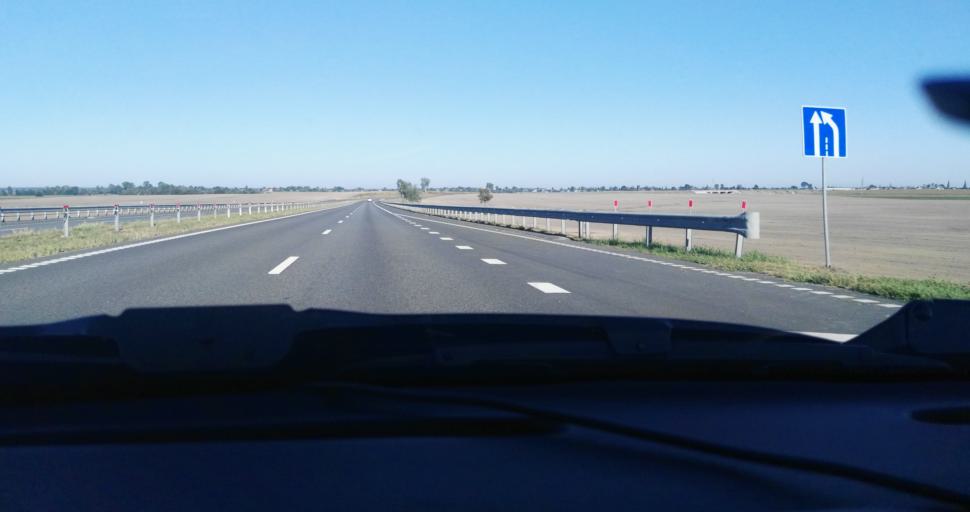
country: BY
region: Gomel
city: Buda-Kashalyova
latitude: 52.5058
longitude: 30.6427
